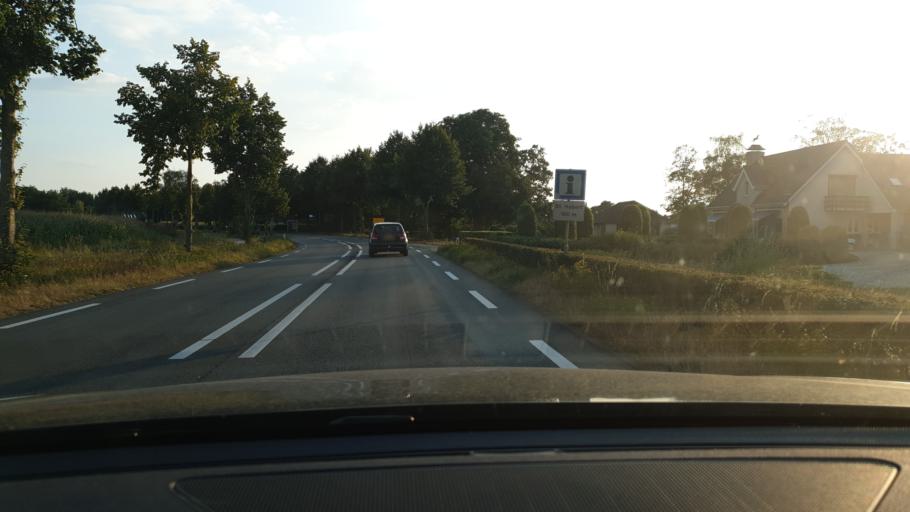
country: NL
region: North Brabant
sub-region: Gemeente Mill en Sint Hubert
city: Wilbertoord
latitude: 51.6794
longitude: 5.8172
